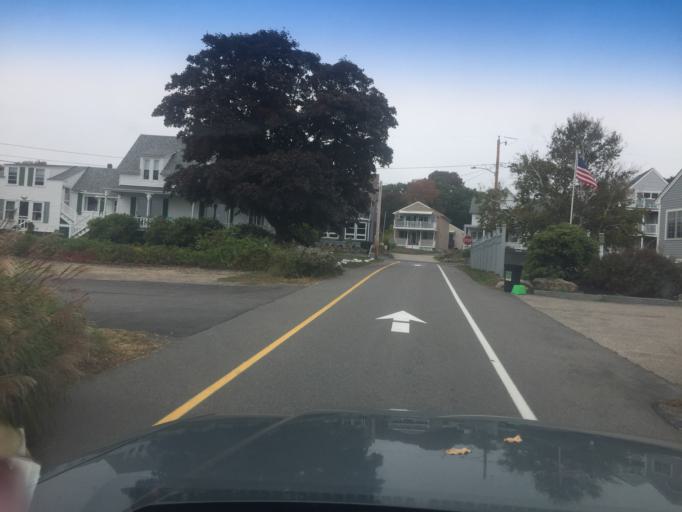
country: US
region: Maine
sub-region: York County
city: York Beach
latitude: 43.1767
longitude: -70.6084
